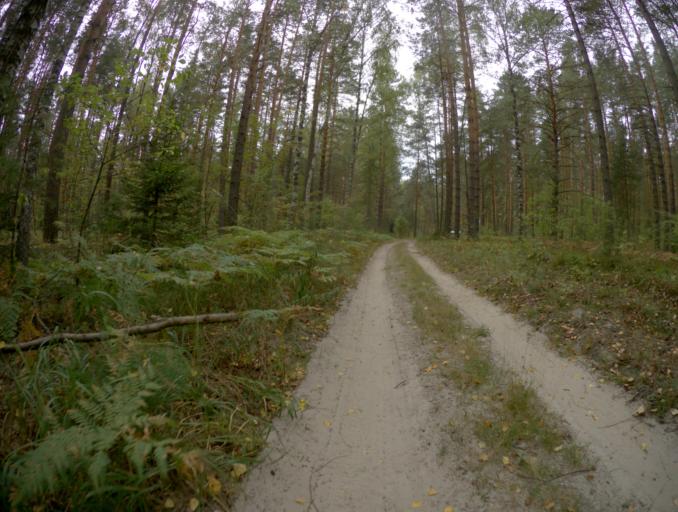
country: RU
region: Vladimir
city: Ivanishchi
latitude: 55.8486
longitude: 40.3495
